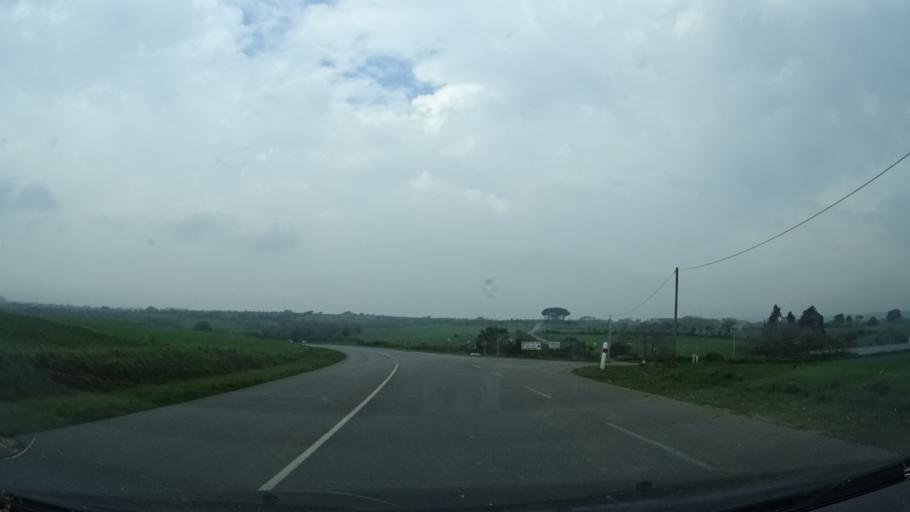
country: FR
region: Brittany
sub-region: Departement du Finistere
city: Plouarzel
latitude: 48.4371
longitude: -4.7161
